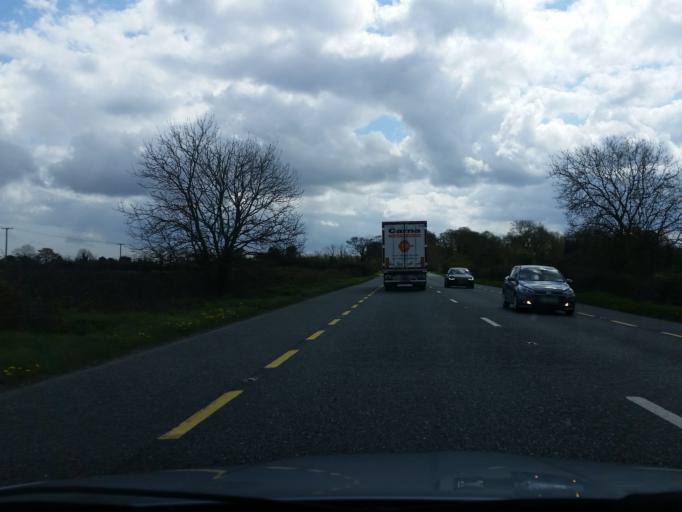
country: IE
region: Leinster
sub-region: An Mhi
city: Ashbourne
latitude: 53.5363
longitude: -6.4240
